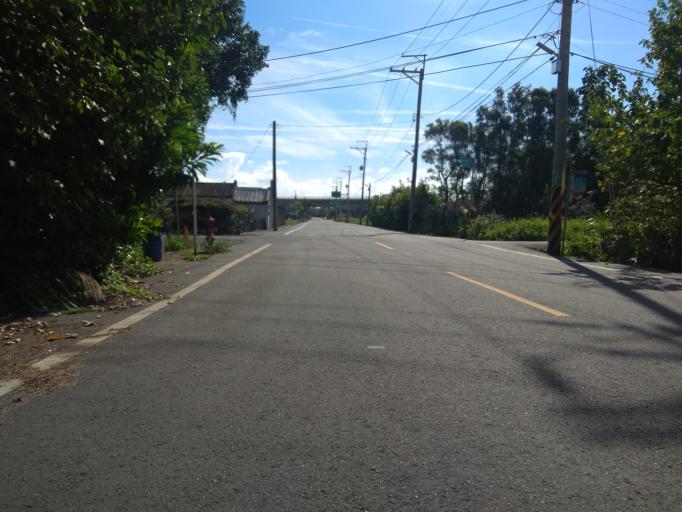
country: TW
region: Taiwan
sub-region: Hsinchu
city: Zhubei
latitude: 25.0148
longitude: 121.0342
